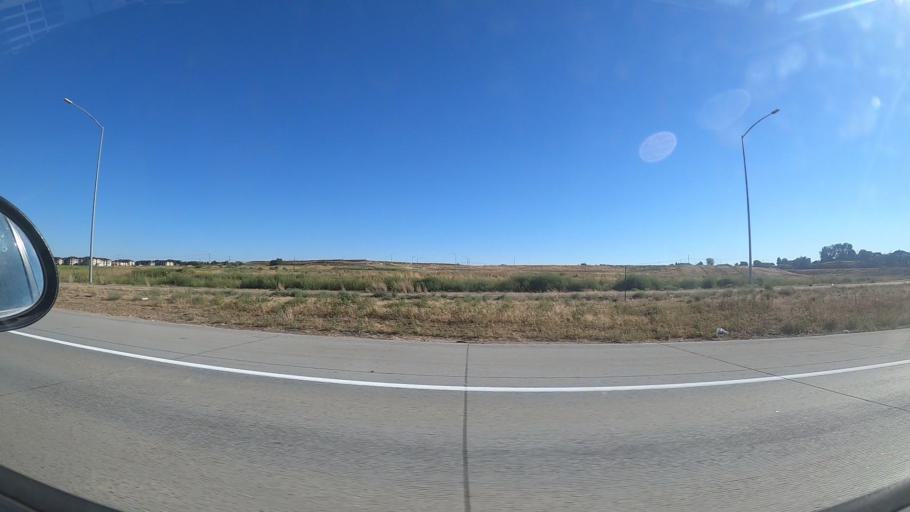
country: US
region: Idaho
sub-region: Ada County
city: Meridian
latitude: 43.5933
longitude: -116.4359
